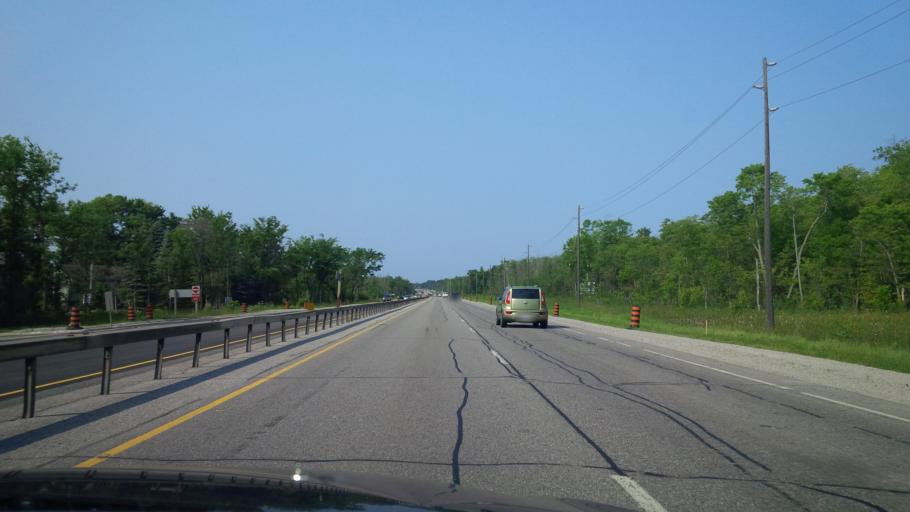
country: CA
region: Ontario
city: Orillia
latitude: 44.7385
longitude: -79.3536
